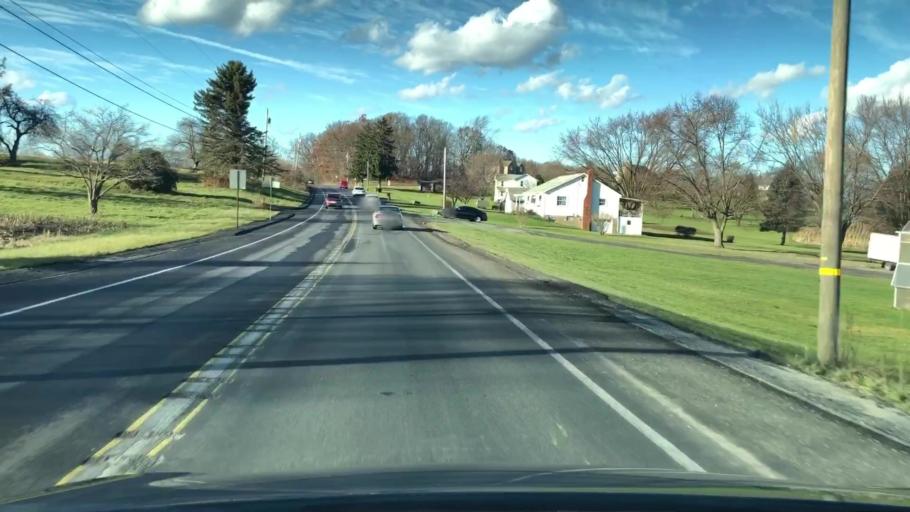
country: US
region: Pennsylvania
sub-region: Butler County
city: Saxonburg
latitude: 40.7619
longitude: -79.7800
